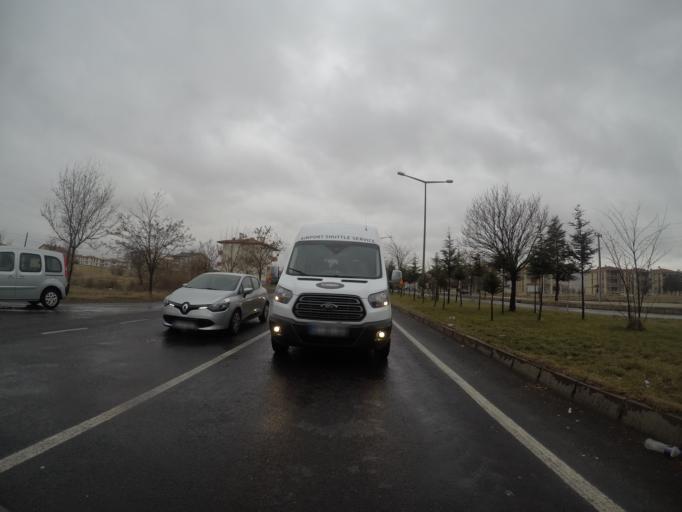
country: TR
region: Nevsehir
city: Avanos
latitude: 38.7047
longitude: 34.8556
